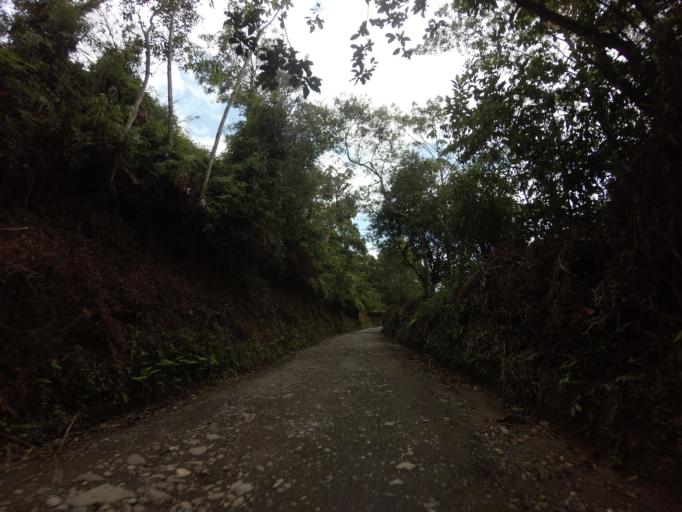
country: CO
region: Caldas
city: Victoria
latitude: 5.3238
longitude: -74.9360
